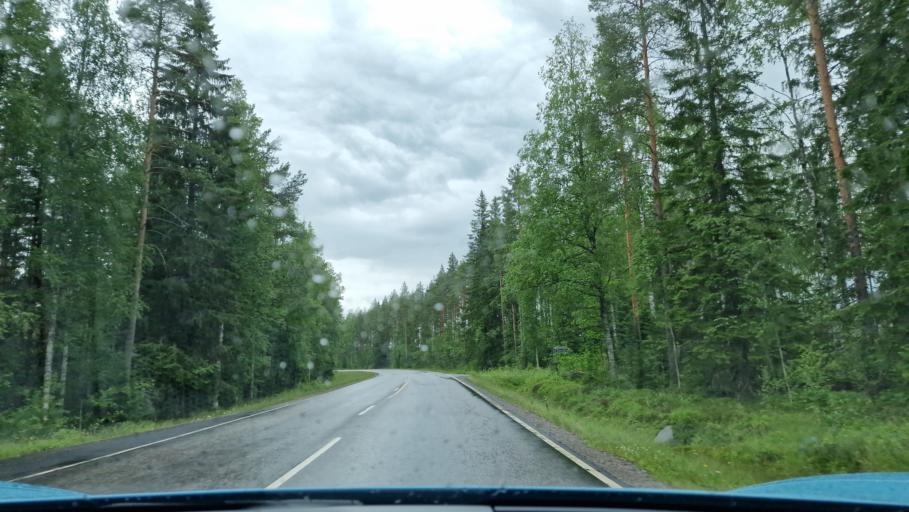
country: FI
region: Central Finland
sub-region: Saarijaervi-Viitasaari
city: Pylkoenmaeki
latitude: 62.6437
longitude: 24.5755
